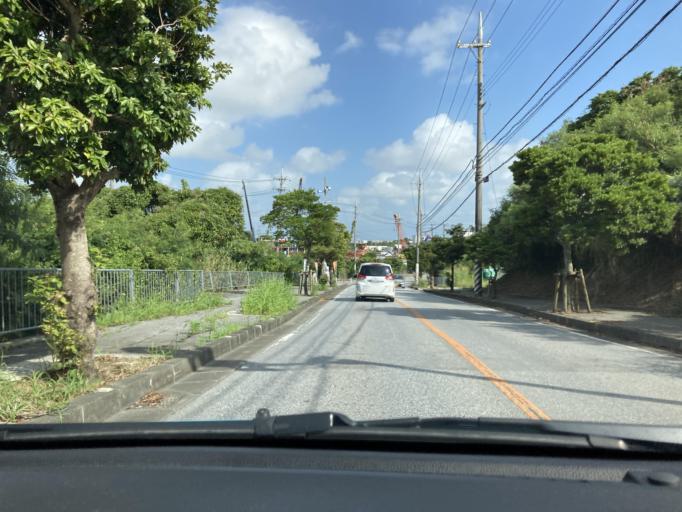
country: JP
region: Okinawa
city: Ginowan
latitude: 26.2588
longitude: 127.7765
